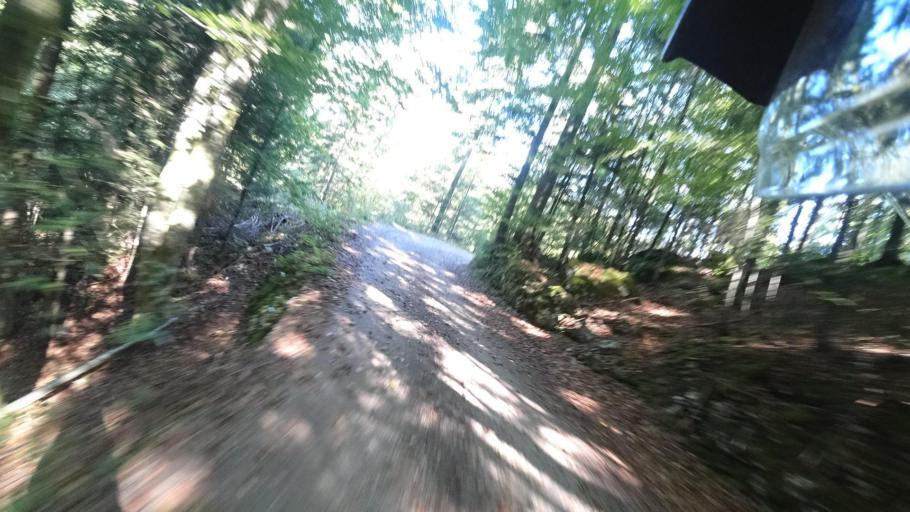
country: HR
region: Primorsko-Goranska
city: Vrbovsko
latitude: 45.2597
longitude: 15.1101
